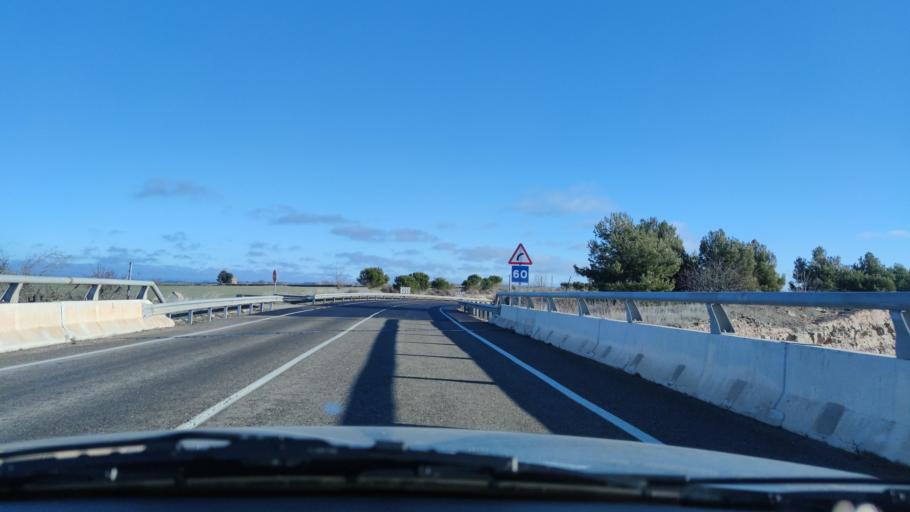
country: ES
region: Catalonia
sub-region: Provincia de Lleida
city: Cervera
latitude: 41.6835
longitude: 1.2945
